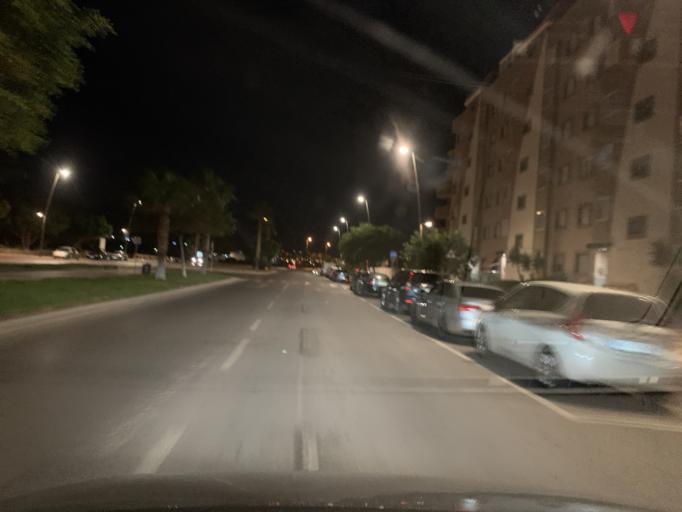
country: ES
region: Andalusia
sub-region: Provincia de Almeria
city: Roquetas de Mar
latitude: 36.7773
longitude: -2.6077
